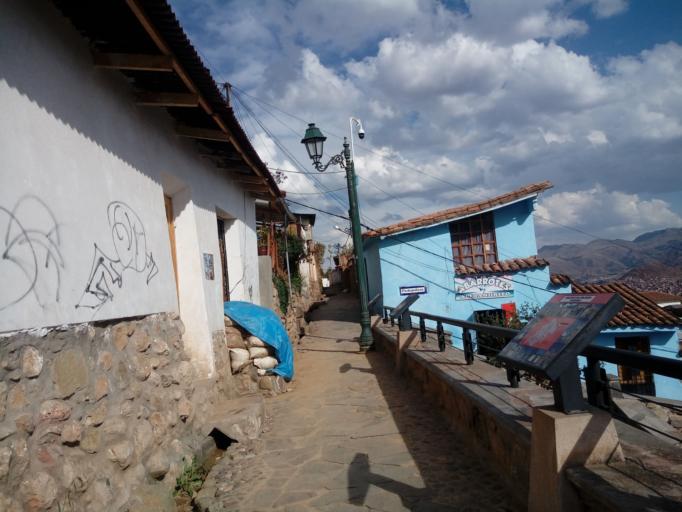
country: PE
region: Cusco
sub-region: Provincia de Cusco
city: Cusco
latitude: -13.5137
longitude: -71.9740
